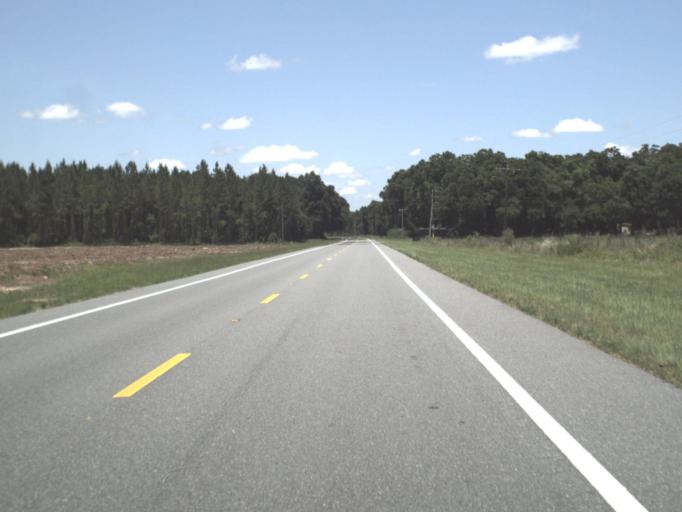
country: US
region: Florida
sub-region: Lafayette County
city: Mayo
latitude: 29.8659
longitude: -82.9590
